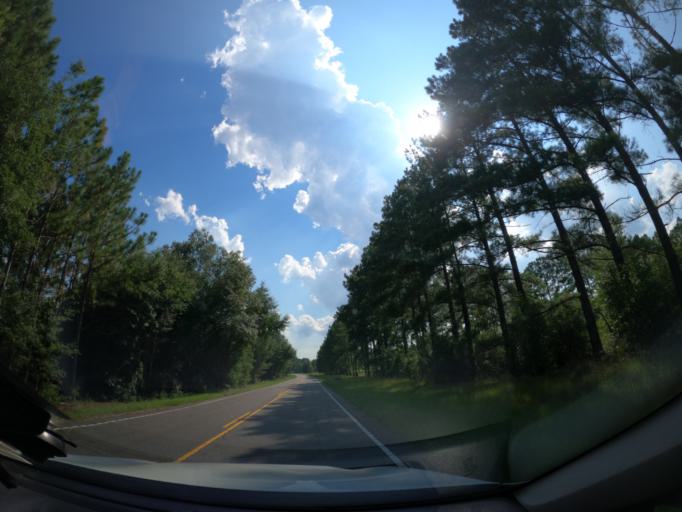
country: US
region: South Carolina
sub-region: Barnwell County
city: Williston
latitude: 33.5225
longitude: -81.4984
